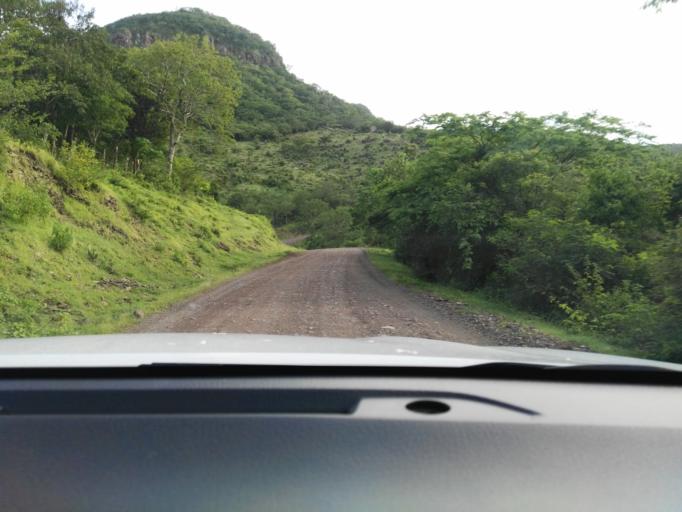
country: NI
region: Matagalpa
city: Ciudad Dario
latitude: 12.8460
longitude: -86.0483
